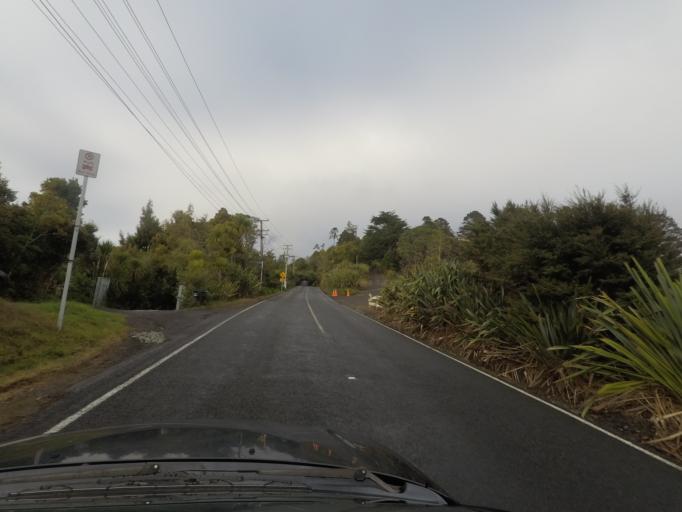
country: NZ
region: Auckland
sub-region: Auckland
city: Titirangi
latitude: -36.9253
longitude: 174.5828
